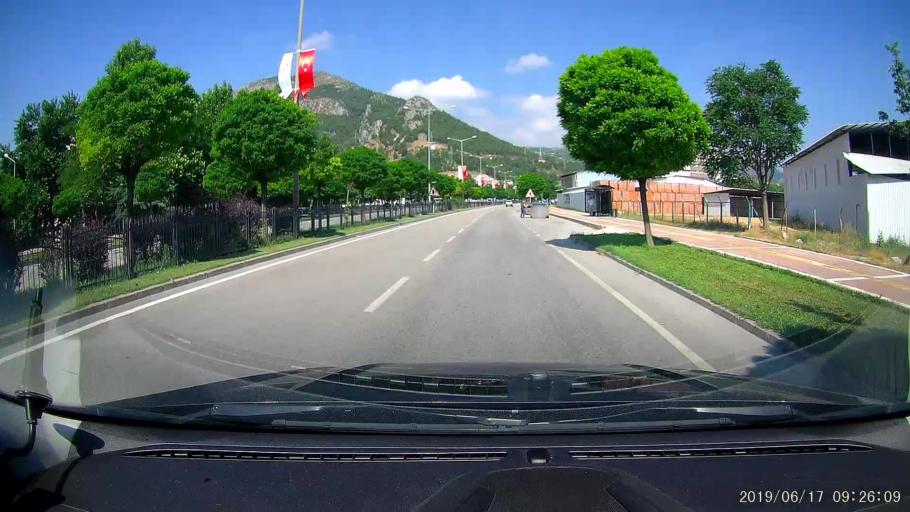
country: TR
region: Amasya
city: Amasya
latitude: 40.6688
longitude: 35.8393
